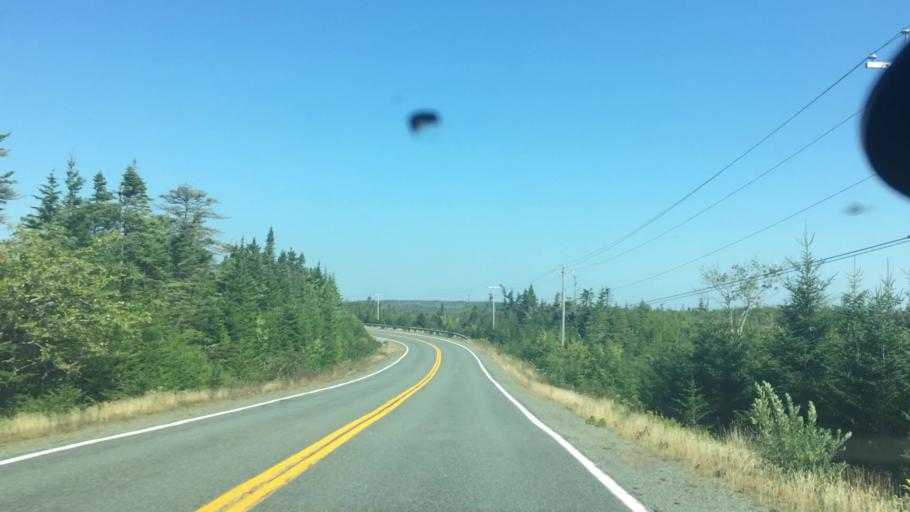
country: CA
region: Nova Scotia
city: Antigonish
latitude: 44.9882
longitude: -62.0963
